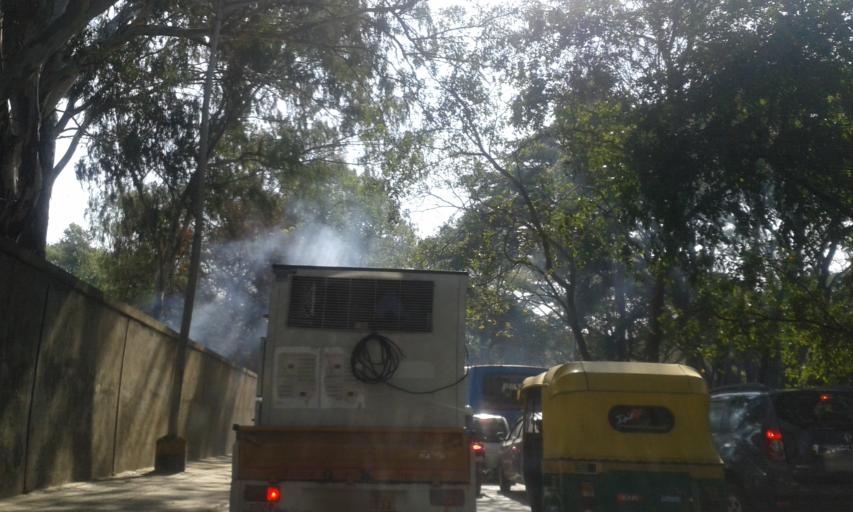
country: IN
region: Karnataka
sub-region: Bangalore Urban
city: Bangalore
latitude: 12.9677
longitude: 77.6153
